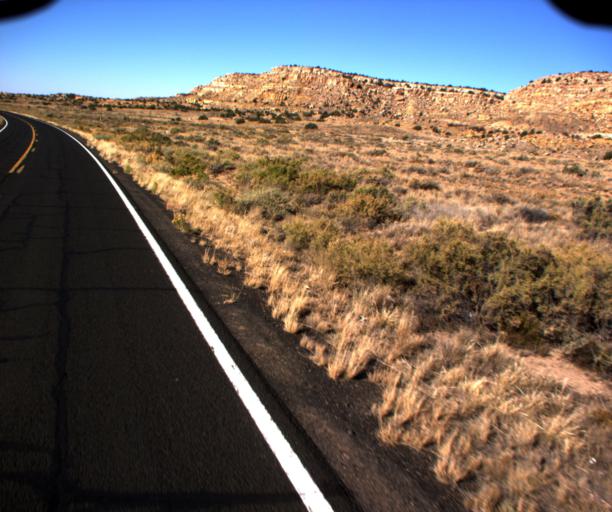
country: US
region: Arizona
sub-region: Navajo County
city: First Mesa
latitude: 35.8403
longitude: -110.2551
